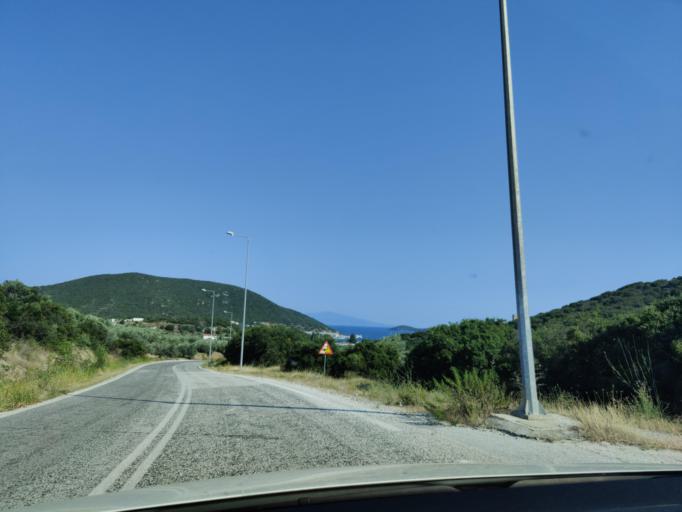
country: GR
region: East Macedonia and Thrace
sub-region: Nomos Kavalas
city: Nea Iraklitsa
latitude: 40.8576
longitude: 24.3083
